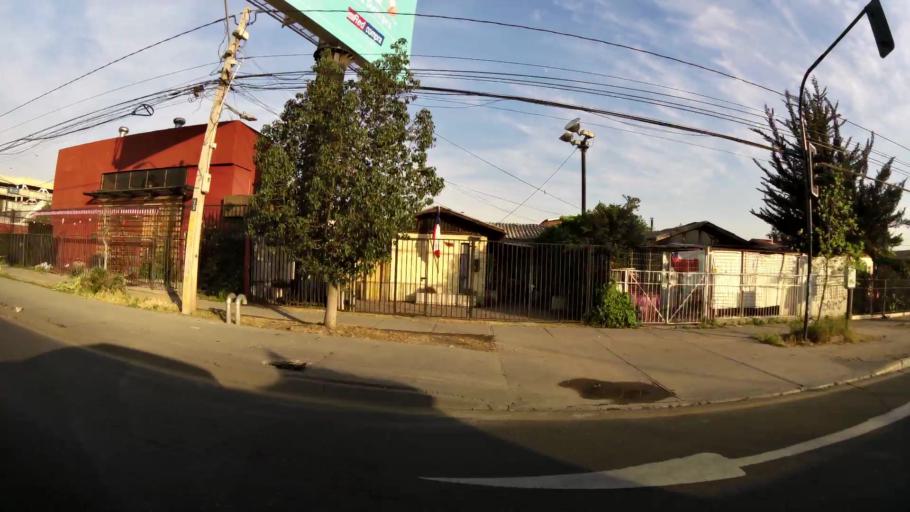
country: CL
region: Santiago Metropolitan
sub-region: Provincia de Santiago
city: Villa Presidente Frei, Nunoa, Santiago, Chile
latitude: -33.5169
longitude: -70.5945
